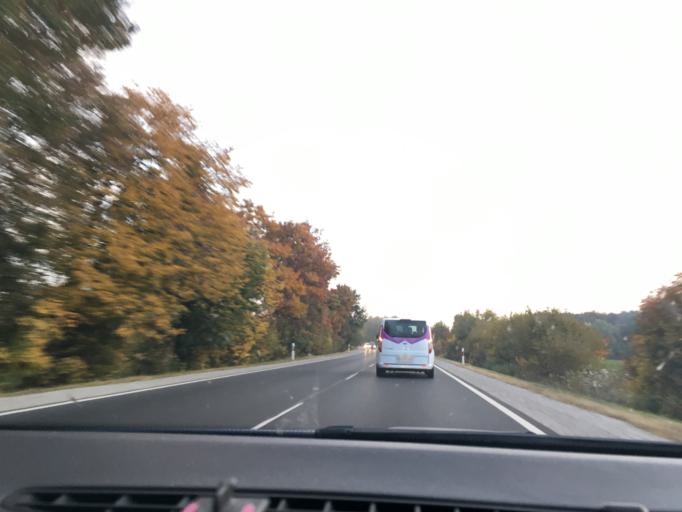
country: HU
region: Hajdu-Bihar
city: Hajduhadhaz
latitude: 47.6778
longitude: 21.6492
